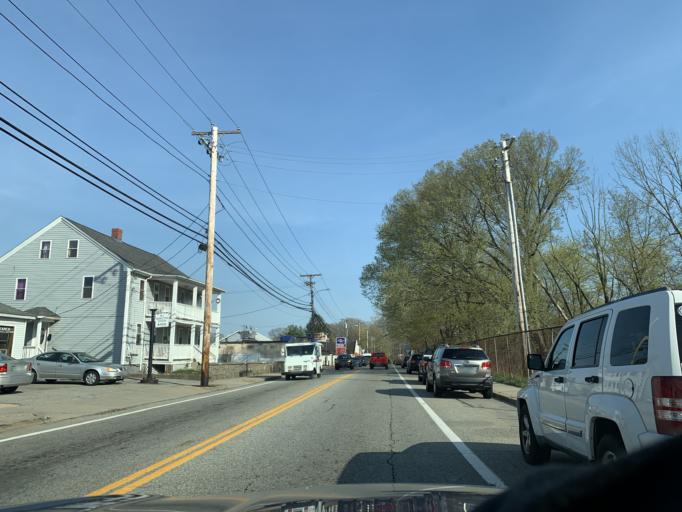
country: US
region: Rhode Island
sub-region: Kent County
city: West Warwick
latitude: 41.7203
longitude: -71.5265
